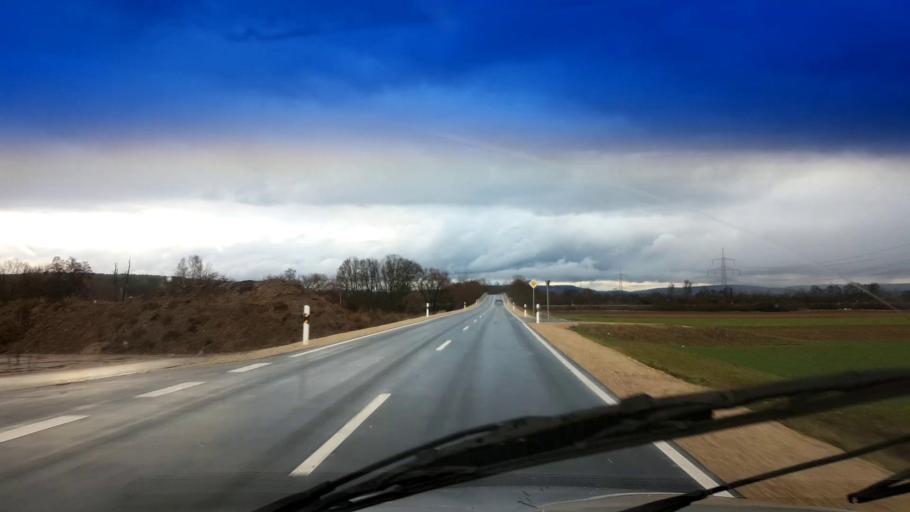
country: DE
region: Bavaria
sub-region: Upper Franconia
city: Gundelsheim
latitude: 49.9359
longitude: 10.9054
